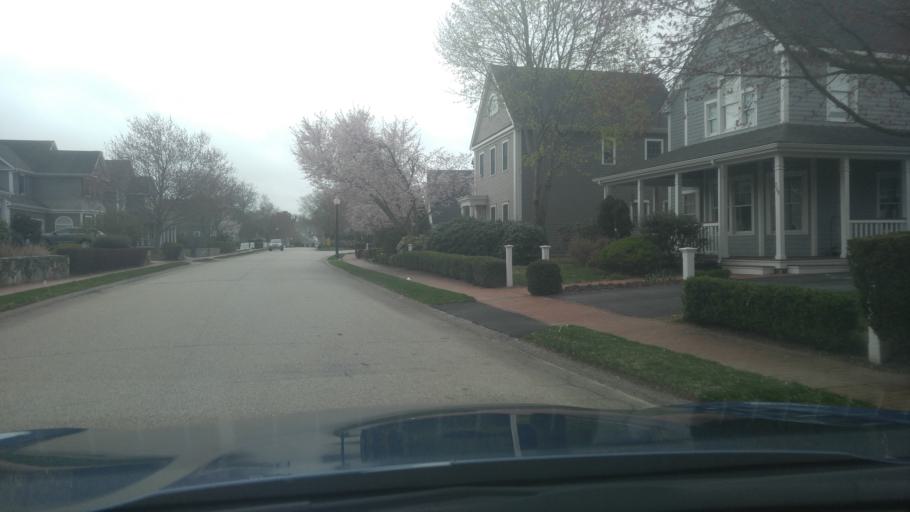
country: US
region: Rhode Island
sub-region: Washington County
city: North Kingstown
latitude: 41.5879
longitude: -71.4461
